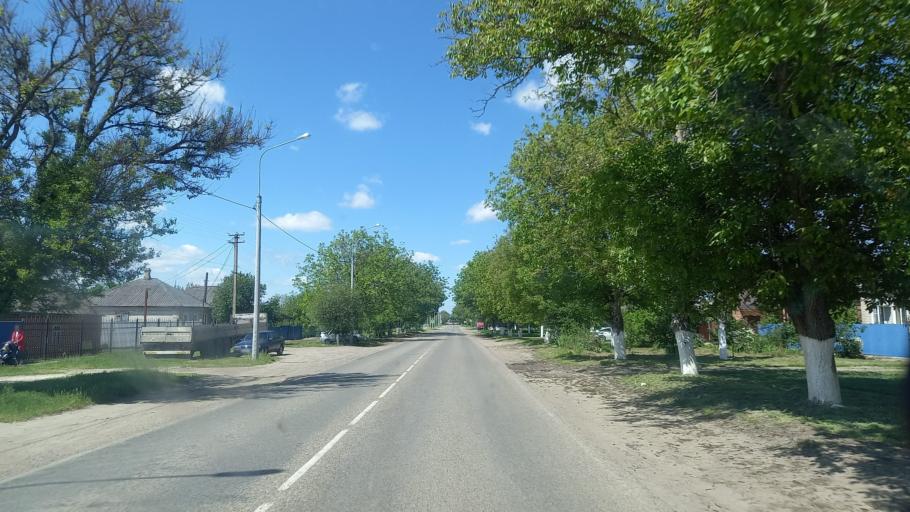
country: RU
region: Krasnodarskiy
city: Novoukrainskoye
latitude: 45.3805
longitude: 40.5100
